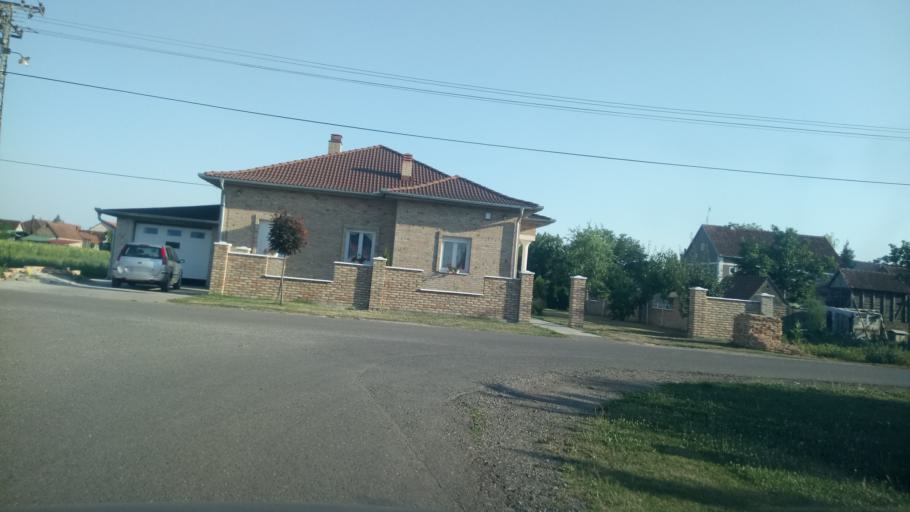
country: RS
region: Autonomna Pokrajina Vojvodina
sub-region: Sremski Okrug
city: Stara Pazova
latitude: 44.9919
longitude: 20.1699
